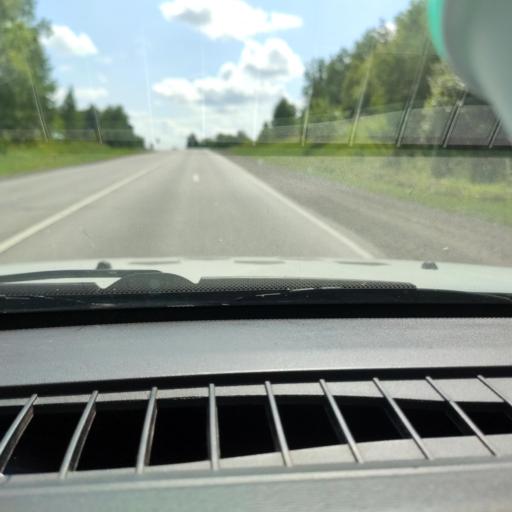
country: RU
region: Bashkortostan
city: Verkhniye Kigi
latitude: 55.3832
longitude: 58.6758
